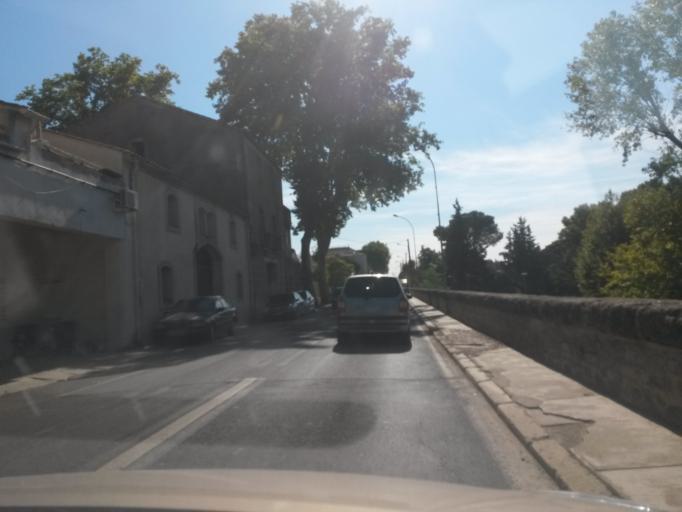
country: FR
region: Languedoc-Roussillon
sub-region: Departement de l'Herault
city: Aniane
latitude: 43.6835
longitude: 3.5829
